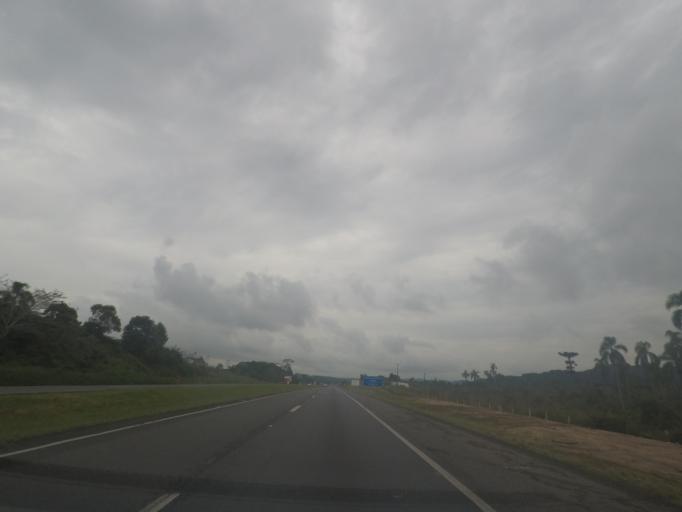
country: BR
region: Sao Paulo
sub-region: Cajati
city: Cajati
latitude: -24.9258
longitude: -48.2665
